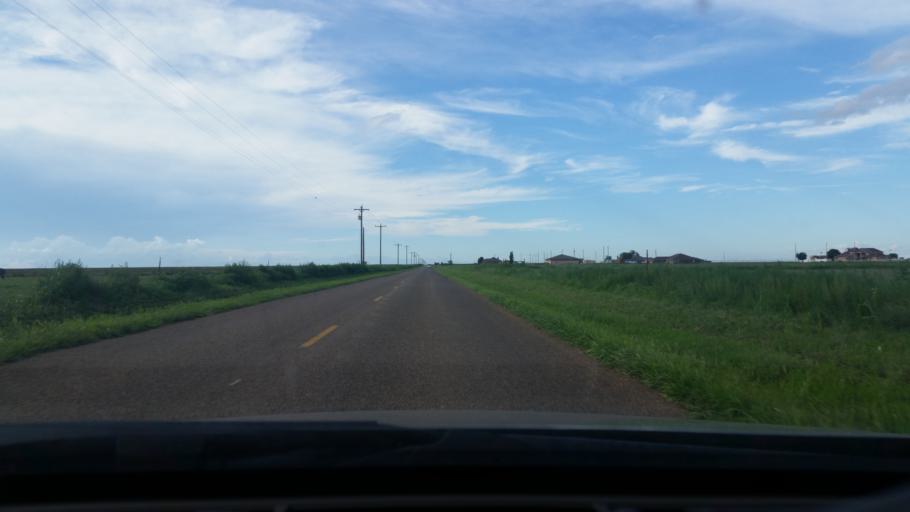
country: US
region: New Mexico
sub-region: Curry County
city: Clovis
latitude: 34.4565
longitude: -103.2140
